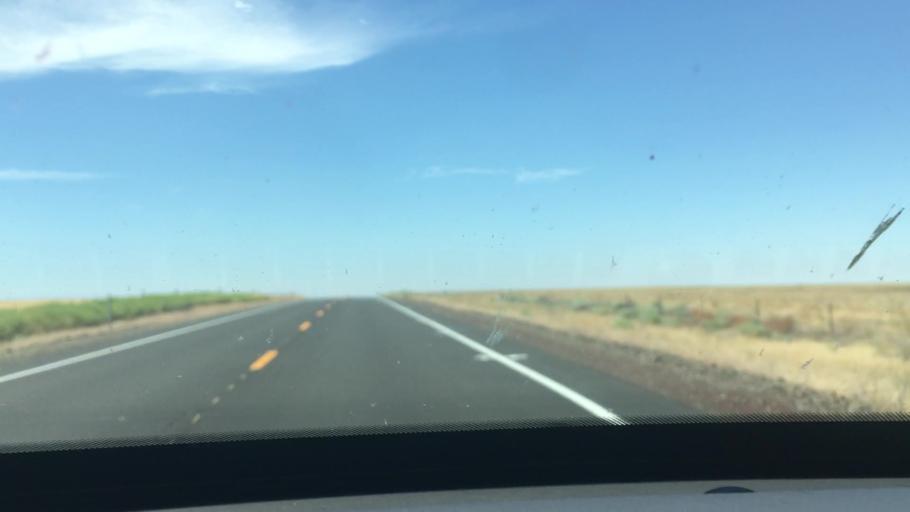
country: US
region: Oregon
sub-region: Sherman County
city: Moro
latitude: 45.2854
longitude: -120.7477
